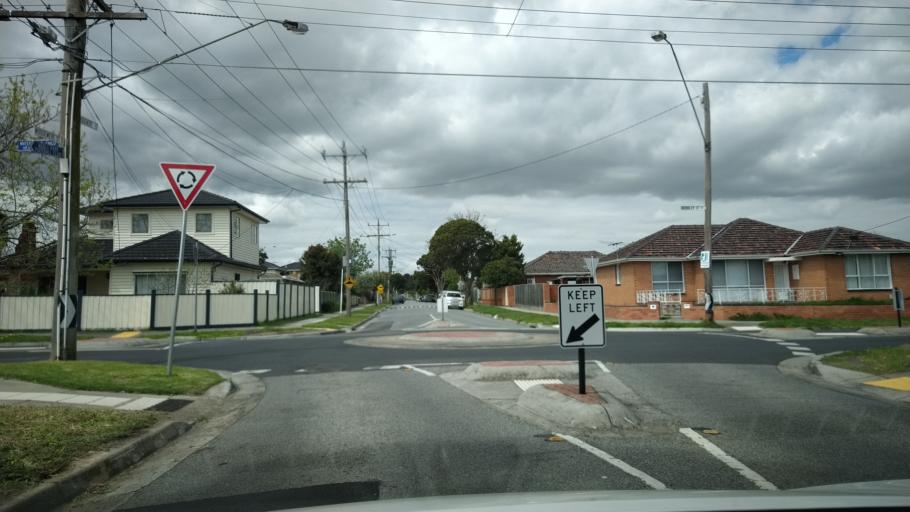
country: AU
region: Victoria
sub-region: Greater Dandenong
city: Noble Park
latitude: -37.9769
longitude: 145.1722
